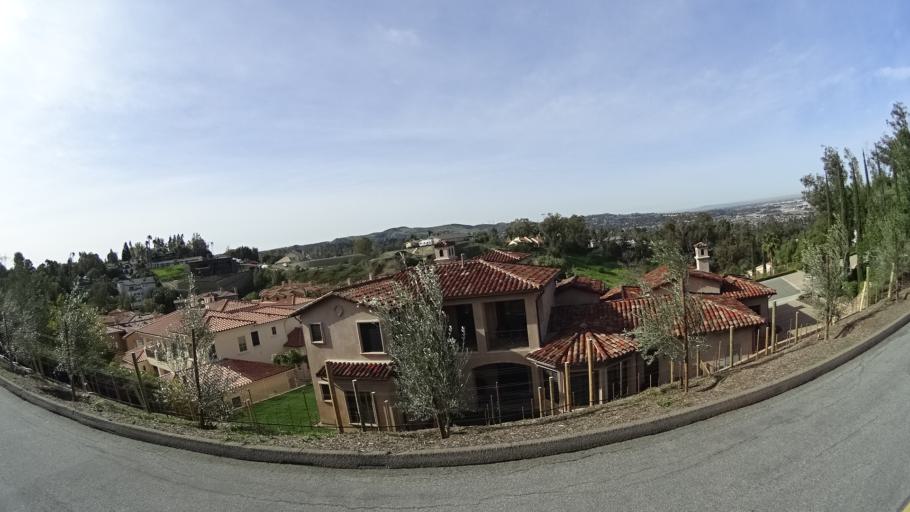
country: US
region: California
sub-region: Orange County
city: Yorba Linda
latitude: 33.8577
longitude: -117.7569
